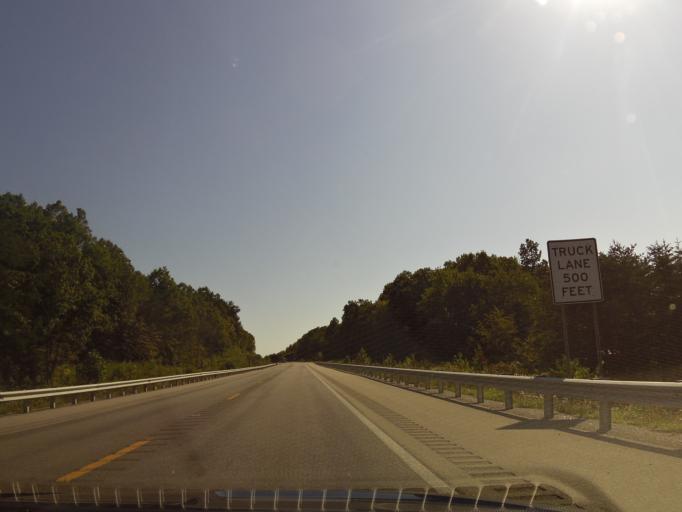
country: US
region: Kentucky
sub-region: Laurel County
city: London
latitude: 37.1078
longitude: -83.9459
